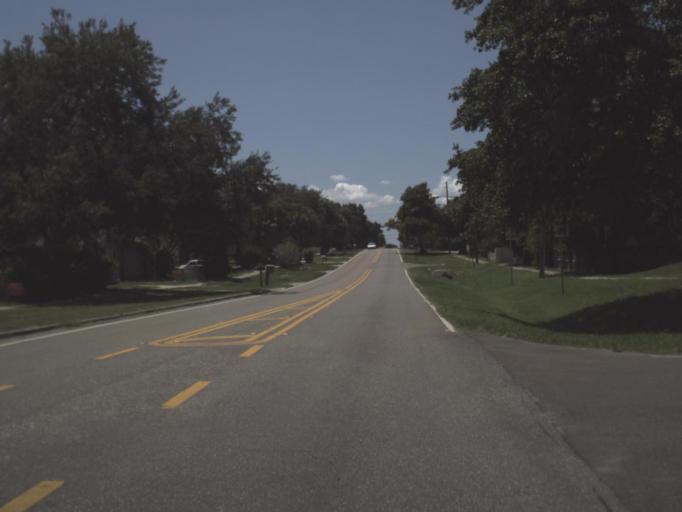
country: US
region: Florida
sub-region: Pinellas County
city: Safety Harbor
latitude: 28.0109
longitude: -82.6841
